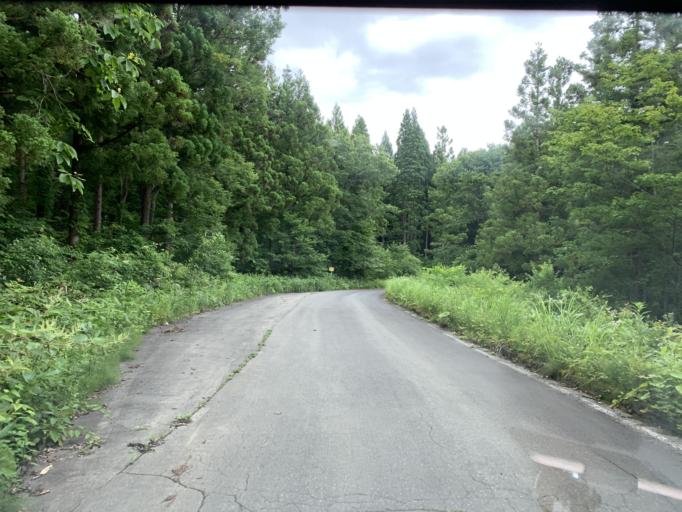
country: JP
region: Iwate
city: Ichinoseki
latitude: 38.9576
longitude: 140.8901
